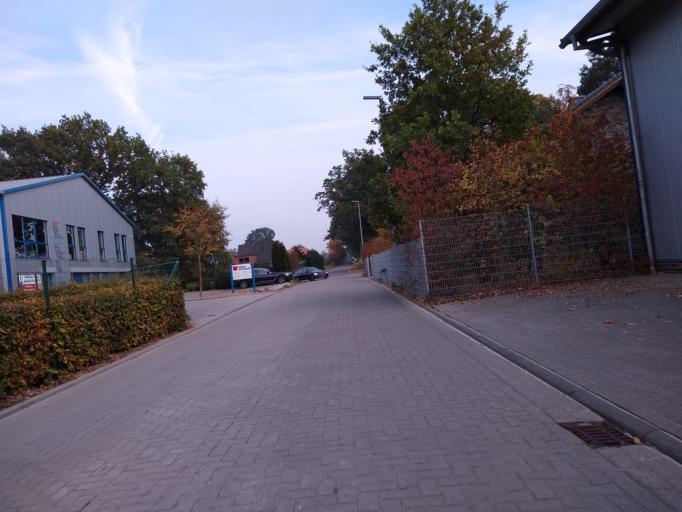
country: DE
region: Lower Saxony
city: Rastede
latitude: 53.2138
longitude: 8.2300
